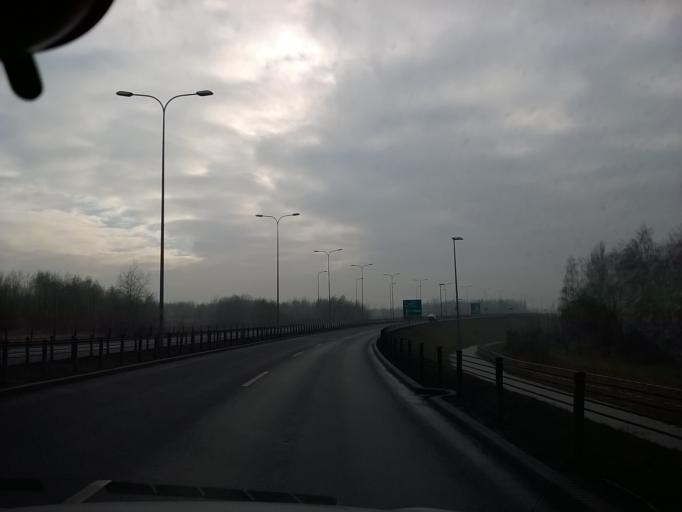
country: PL
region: Silesian Voivodeship
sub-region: Ruda Slaska
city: Ruda Slaska
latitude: 50.2950
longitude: 18.8583
